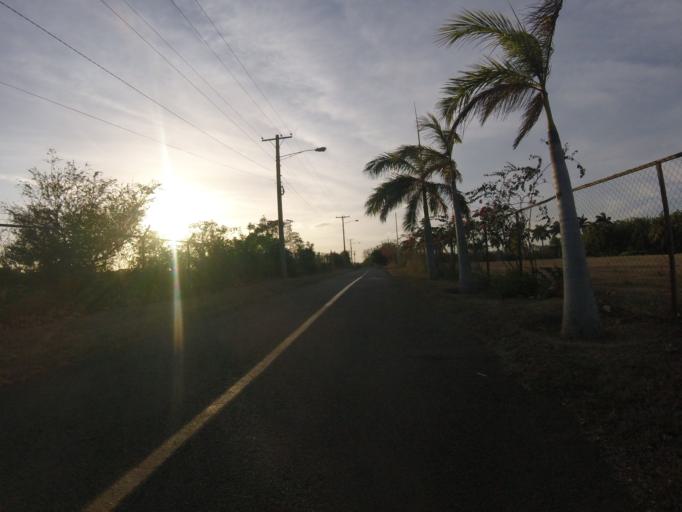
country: NI
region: Masaya
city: Ticuantepe
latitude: 12.0931
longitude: -86.1858
